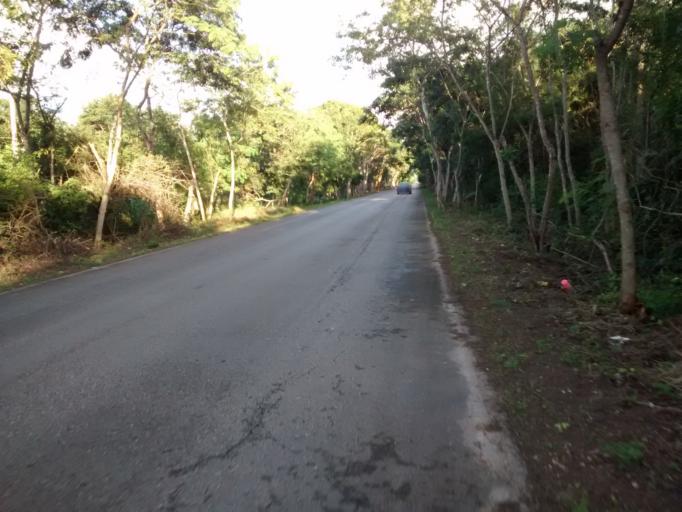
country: MX
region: Yucatan
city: Valladolid
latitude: 20.7312
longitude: -88.2242
